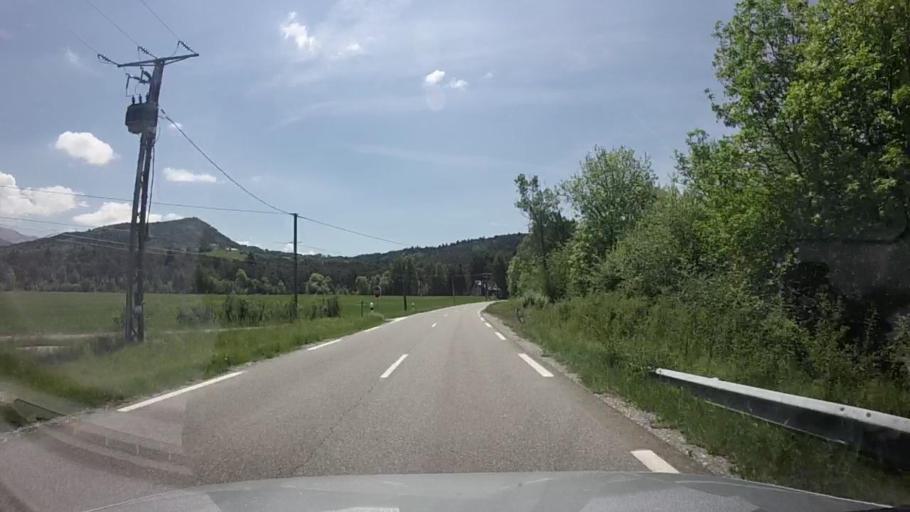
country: FR
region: Provence-Alpes-Cote d'Azur
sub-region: Departement des Alpes-de-Haute-Provence
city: Seyne-les-Alpes
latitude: 44.3801
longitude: 6.3269
